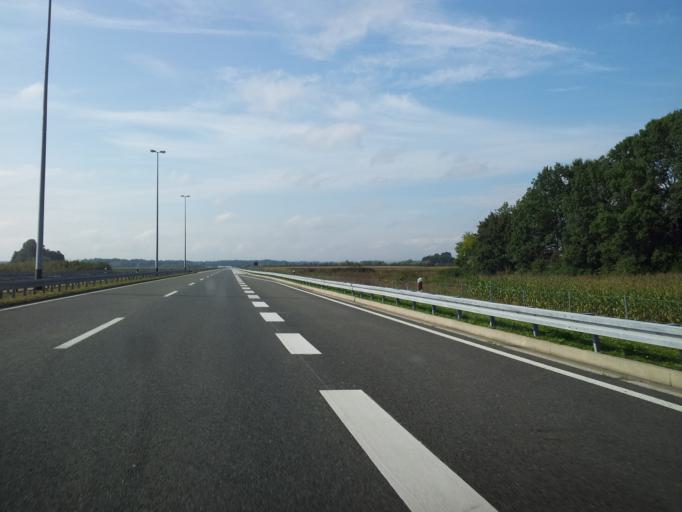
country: HR
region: Brodsko-Posavska
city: Vrpolje
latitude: 45.1817
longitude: 18.3256
